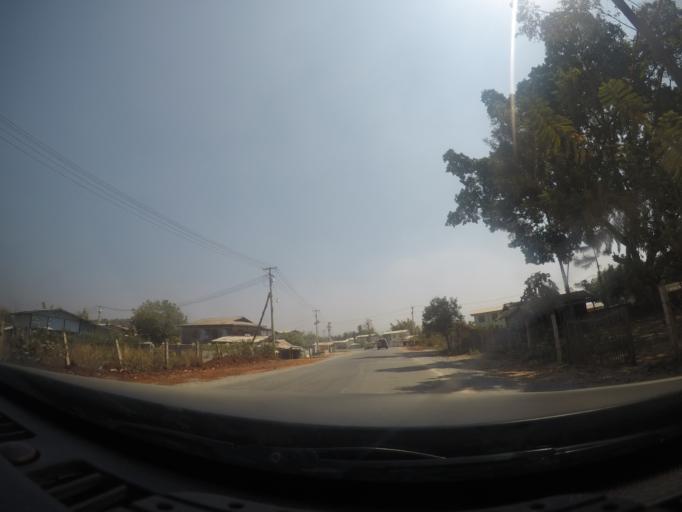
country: MM
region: Shan
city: Taunggyi
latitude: 20.7790
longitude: 97.1486
